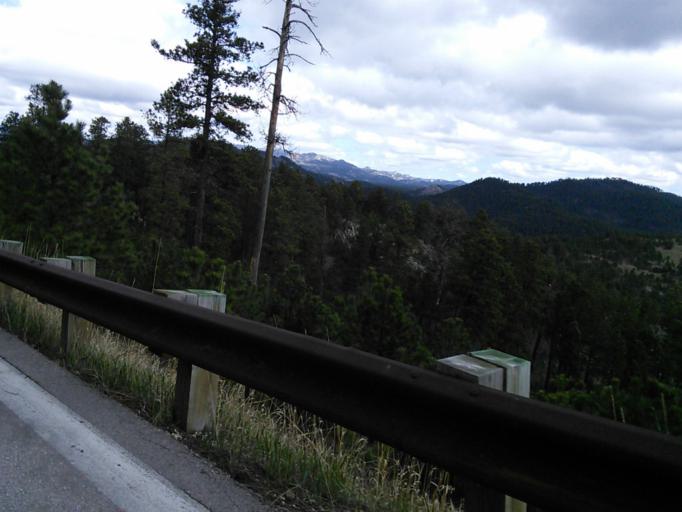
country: US
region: South Dakota
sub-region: Custer County
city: Custer
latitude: 43.7517
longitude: -103.4750
